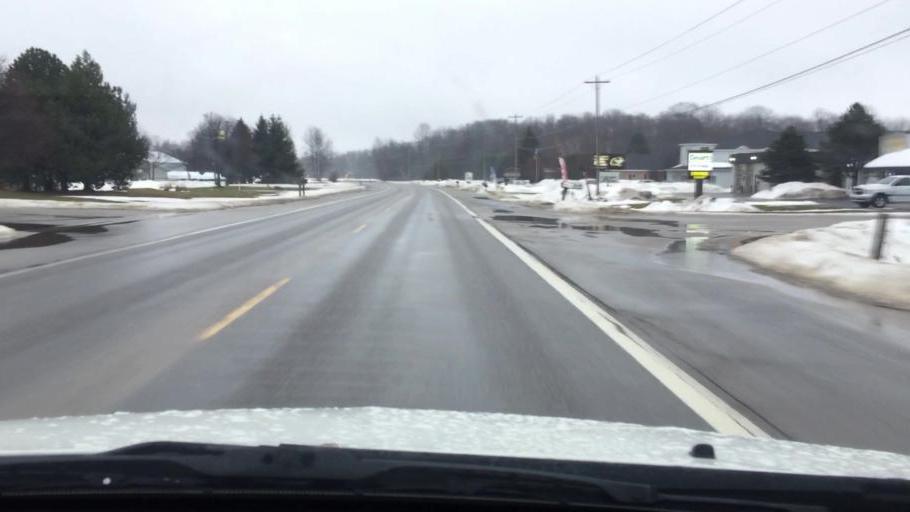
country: US
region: Michigan
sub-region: Charlevoix County
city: Charlevoix
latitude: 45.2987
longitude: -85.2561
